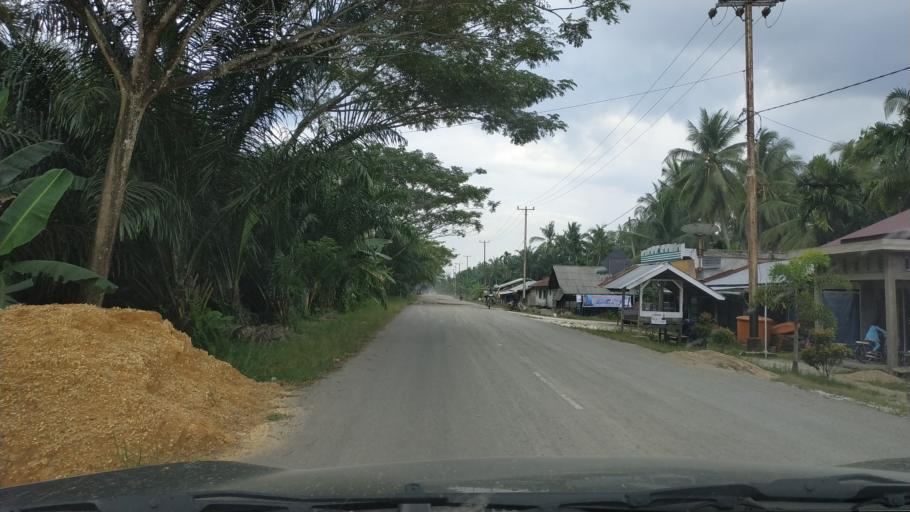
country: ID
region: Riau
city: Sungaisalak
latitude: -0.5658
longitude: 102.9725
